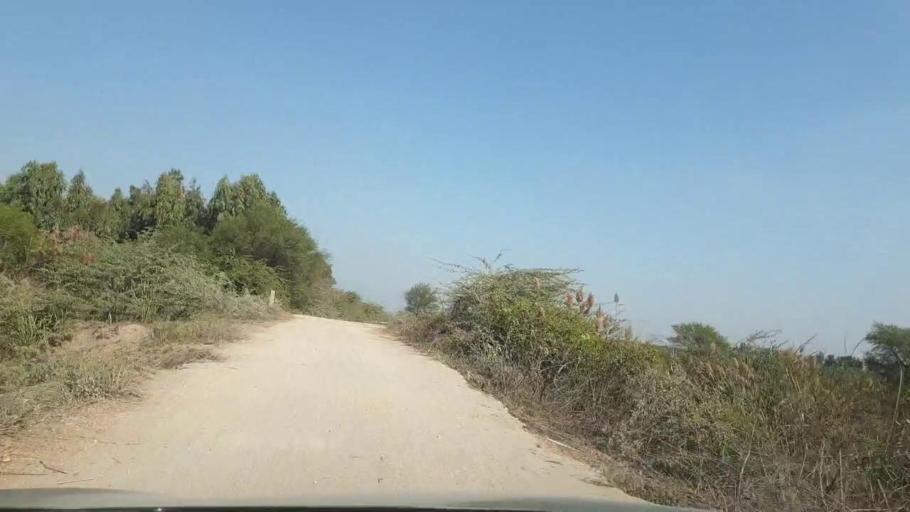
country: PK
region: Sindh
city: Tando Adam
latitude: 25.6260
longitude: 68.6459
